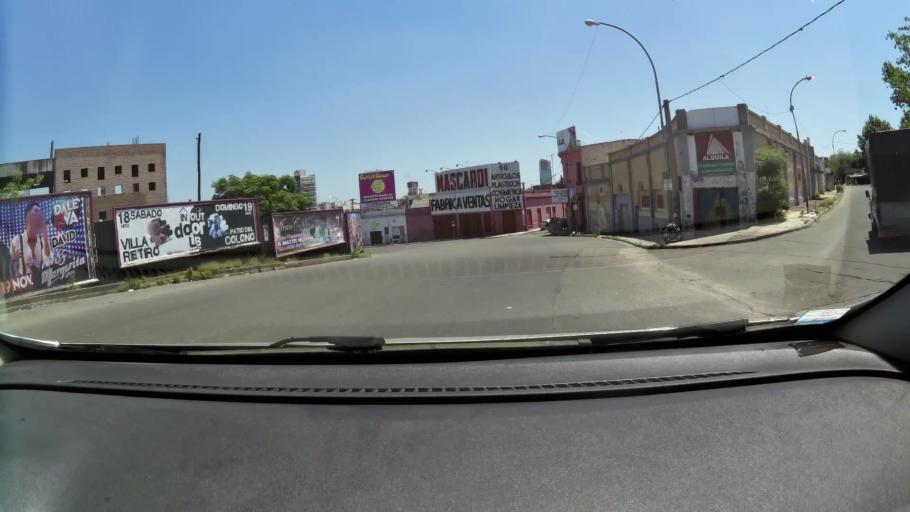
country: AR
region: Cordoba
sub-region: Departamento de Capital
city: Cordoba
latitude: -31.4058
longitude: -64.1763
